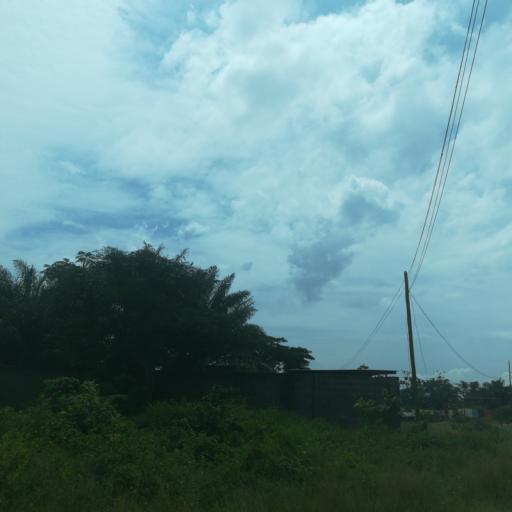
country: NG
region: Lagos
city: Ejirin
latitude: 6.6289
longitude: 3.7077
